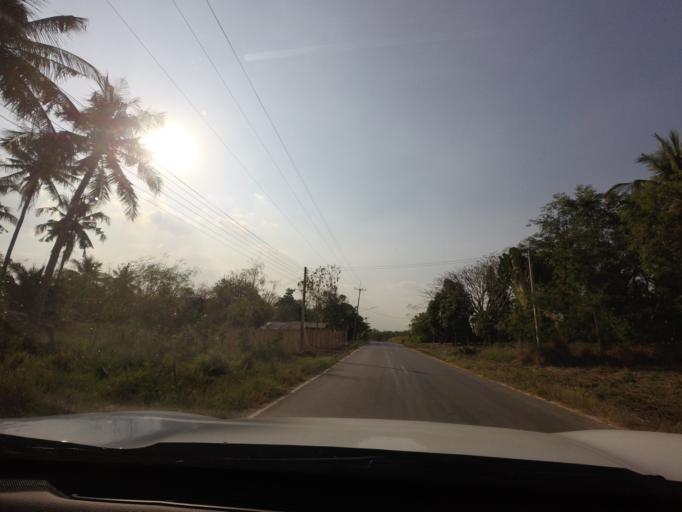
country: TH
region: Nakhon Ratchasima
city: Pak Chong
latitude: 14.6258
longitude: 101.4578
